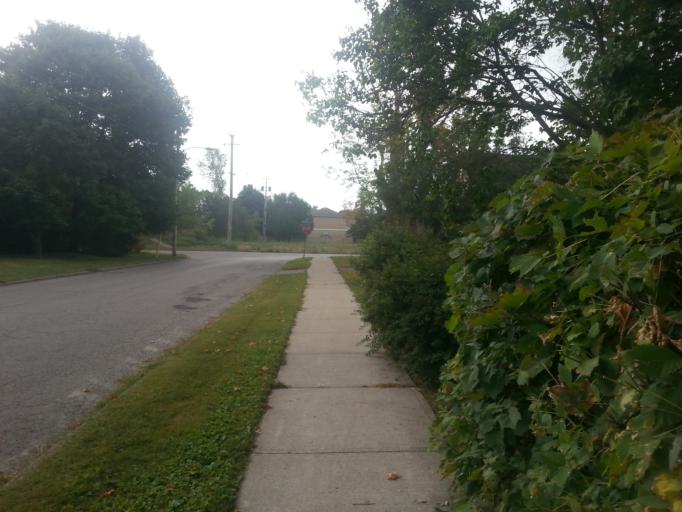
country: CA
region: Ontario
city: Omemee
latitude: 44.3523
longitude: -78.7269
